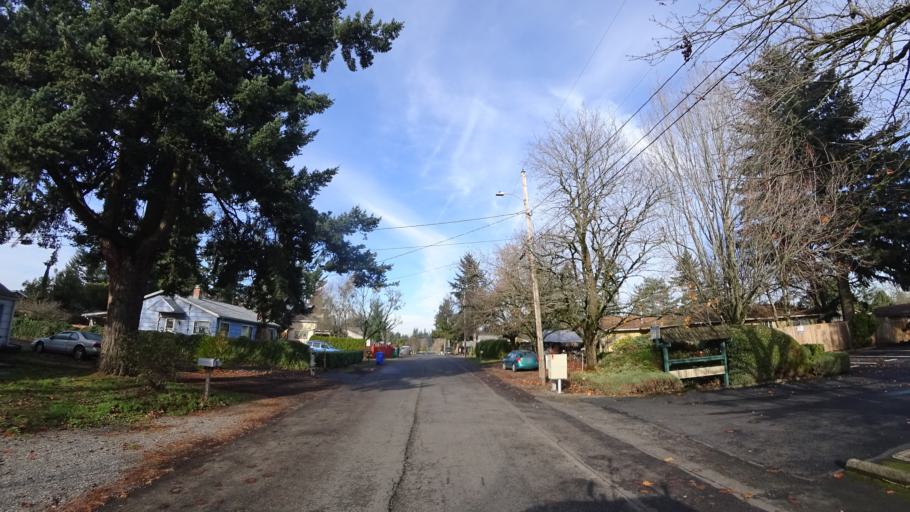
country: US
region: Oregon
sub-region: Multnomah County
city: Lents
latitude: 45.5201
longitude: -122.5261
